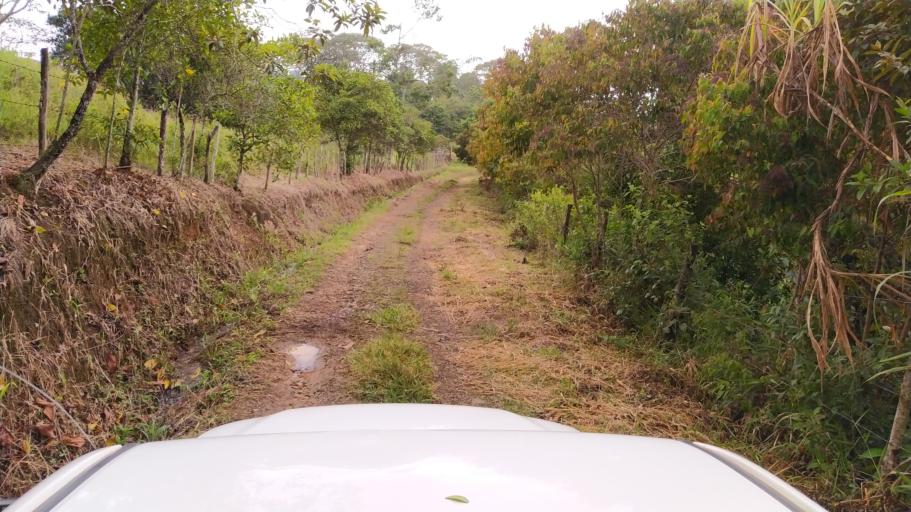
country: CO
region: Valle del Cauca
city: Jamundi
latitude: 3.3230
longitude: -76.5848
